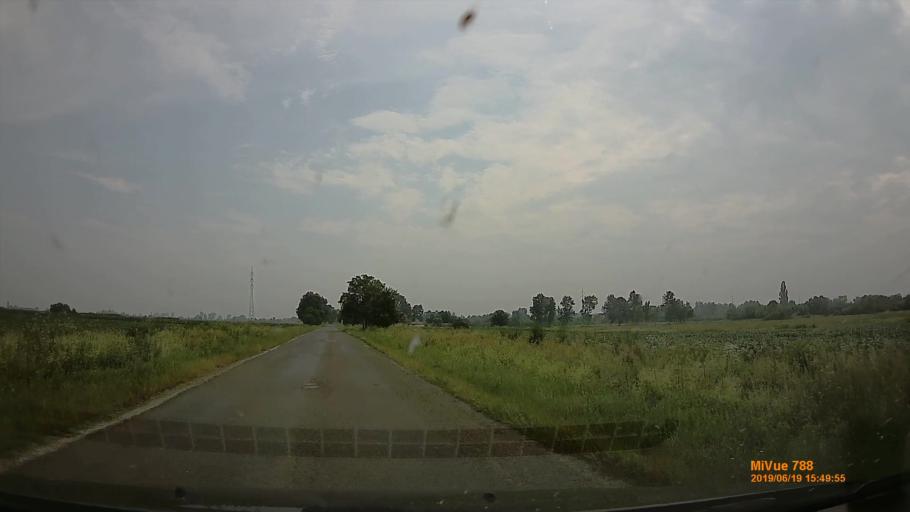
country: HU
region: Baranya
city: Szigetvar
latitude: 46.0388
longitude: 17.7483
